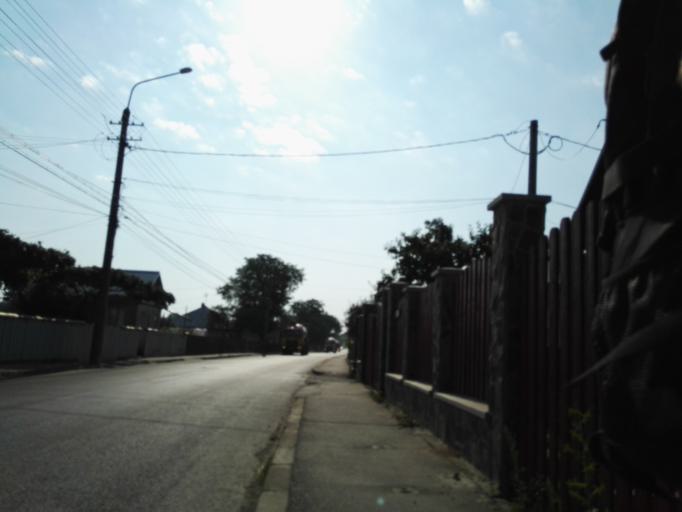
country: RO
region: Suceava
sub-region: Comuna Radaseni
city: Radaseni
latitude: 47.4681
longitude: 26.2775
